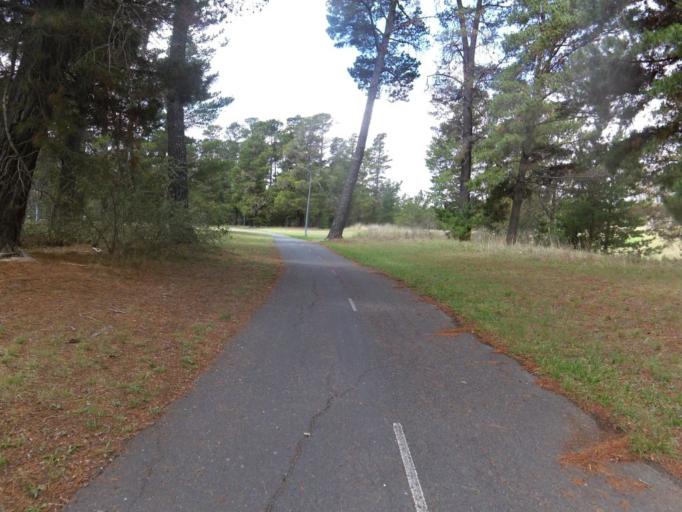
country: AU
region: Australian Capital Territory
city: Macarthur
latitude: -35.4142
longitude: 149.1161
